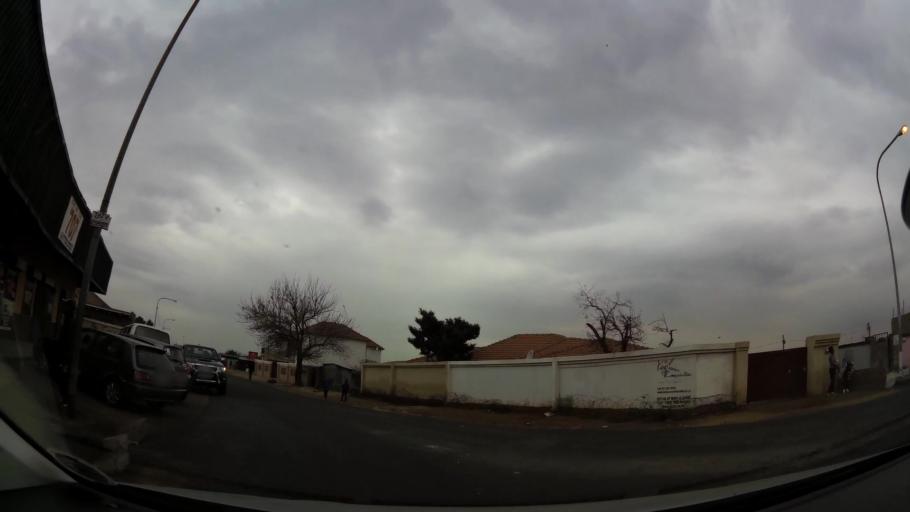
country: ZA
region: Gauteng
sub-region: City of Johannesburg Metropolitan Municipality
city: Soweto
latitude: -26.2556
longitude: 27.8747
